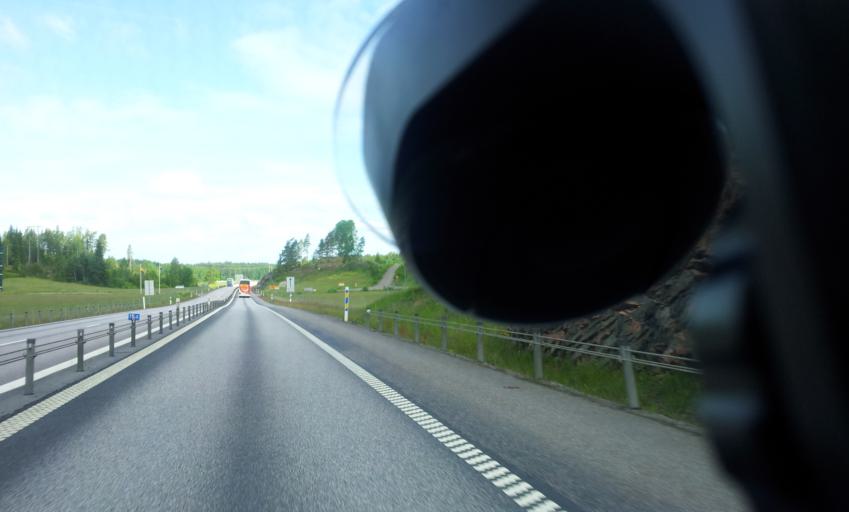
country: SE
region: OEstergoetland
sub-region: Valdemarsviks Kommun
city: Valdemarsvik
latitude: 58.2385
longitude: 16.5459
